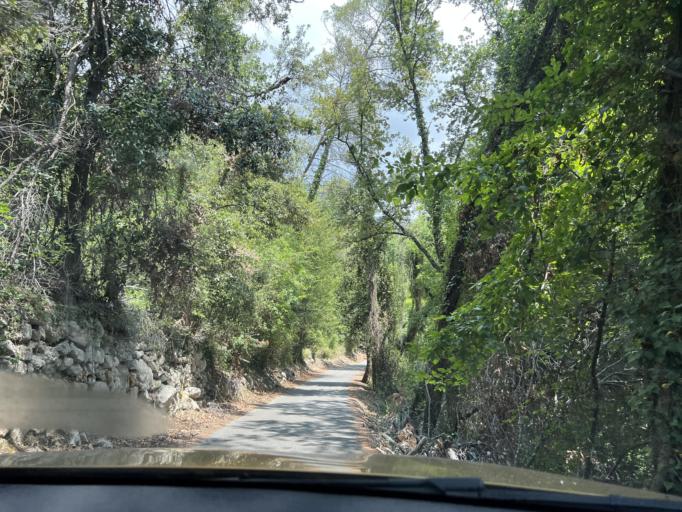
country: FR
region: Provence-Alpes-Cote d'Azur
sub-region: Departement des Alpes-Maritimes
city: Le Rouret
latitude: 43.7028
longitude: 7.0200
